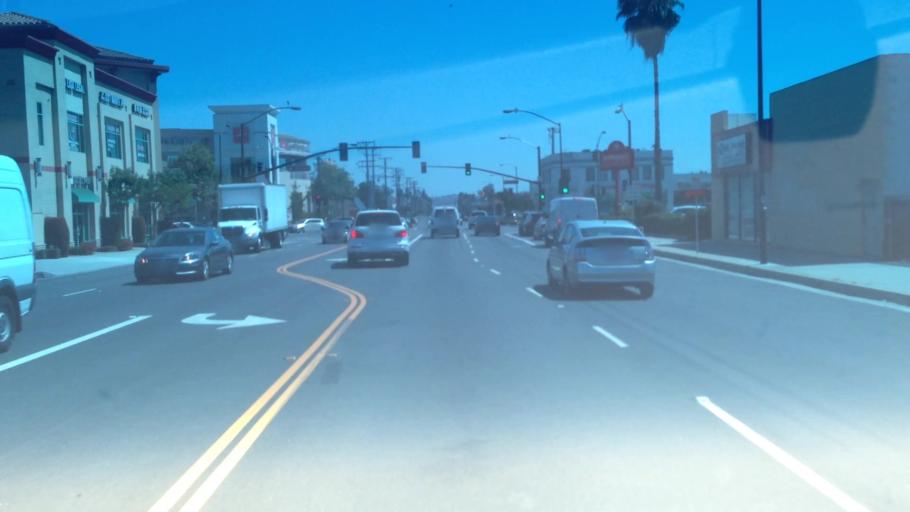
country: US
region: California
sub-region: Los Angeles County
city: East San Gabriel
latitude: 34.0810
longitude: -118.0909
